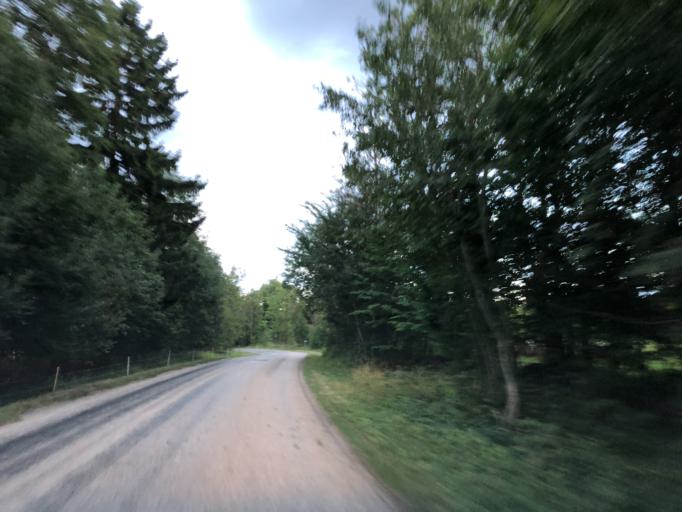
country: EE
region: Laeaene
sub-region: Ridala Parish
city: Uuemoisa
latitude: 58.8785
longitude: 23.6380
